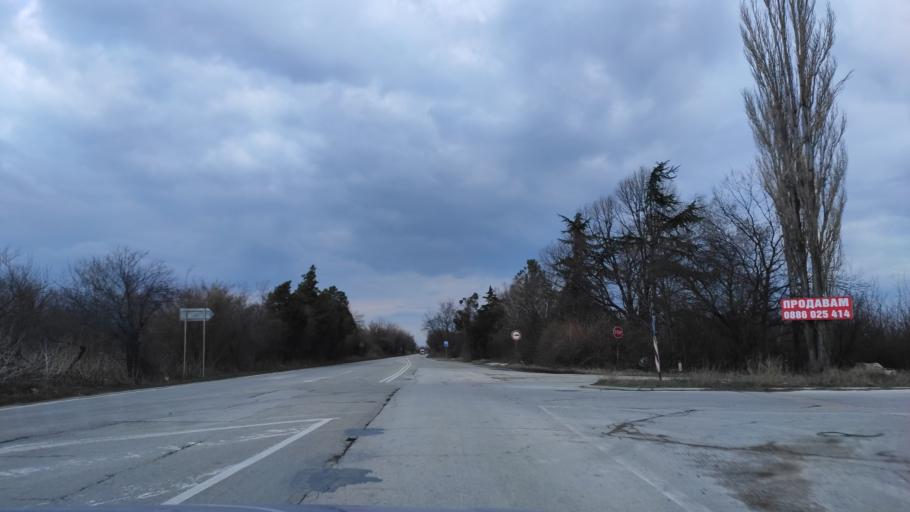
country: BG
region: Varna
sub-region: Obshtina Aksakovo
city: Aksakovo
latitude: 43.2294
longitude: 27.8234
